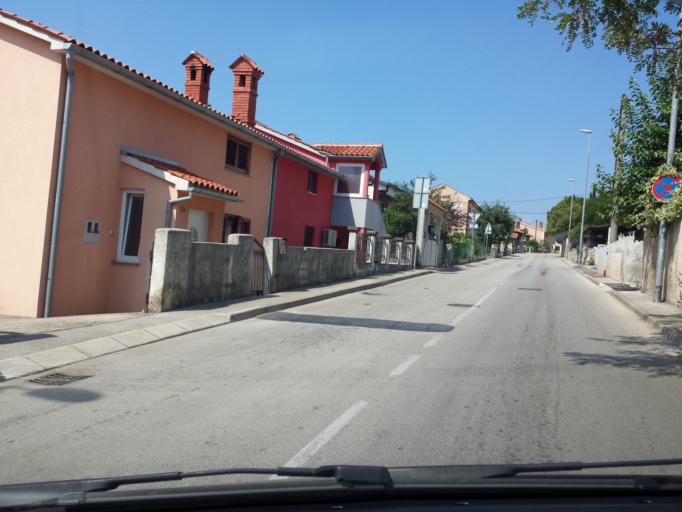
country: HR
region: Istarska
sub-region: Grad Pula
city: Pula
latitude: 44.8898
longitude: 13.8500
